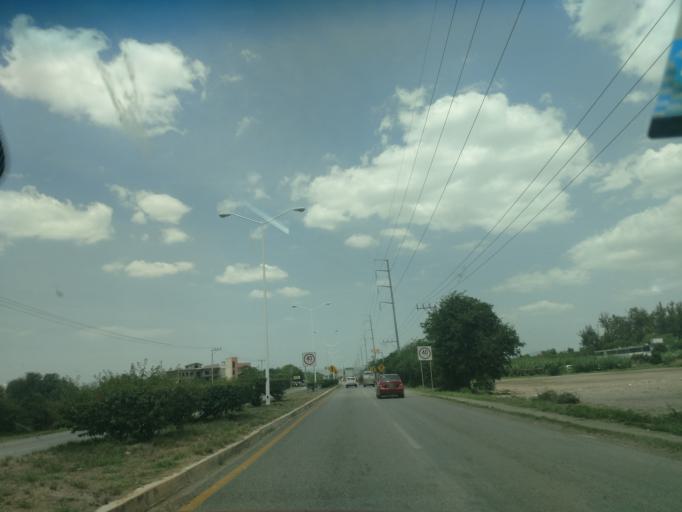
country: MX
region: San Luis Potosi
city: Rio Verde
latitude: 21.9225
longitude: -99.9835
